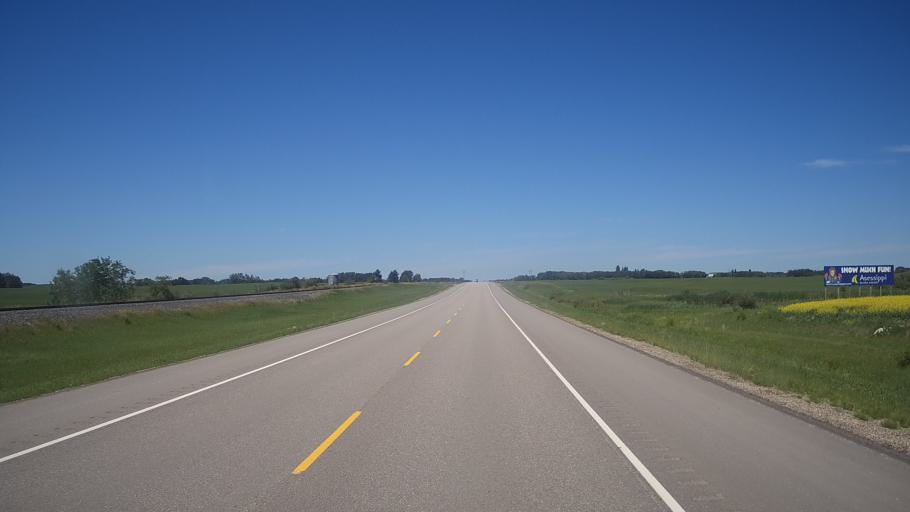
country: CA
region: Manitoba
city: Minnedosa
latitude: 50.2736
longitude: -99.9419
